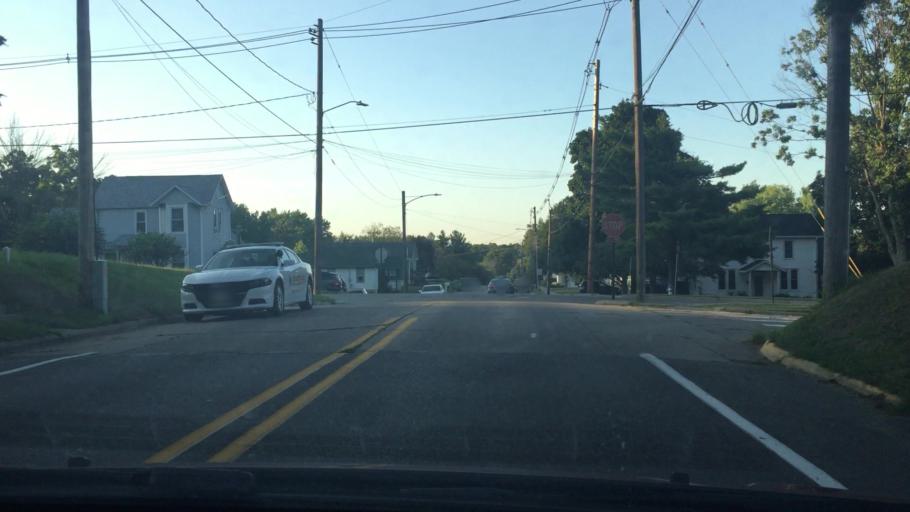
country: US
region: Iowa
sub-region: Muscatine County
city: Muscatine
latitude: 41.4304
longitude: -91.0649
